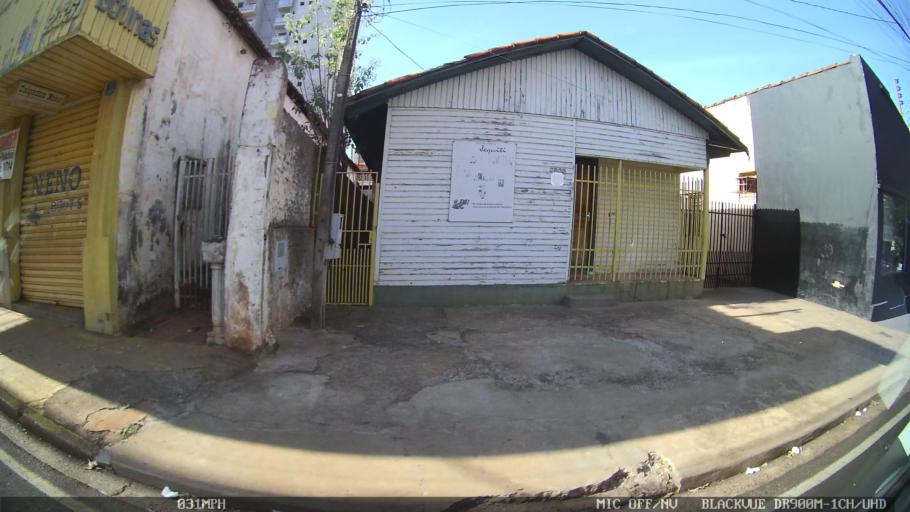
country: BR
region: Sao Paulo
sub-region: Sao Jose Do Rio Preto
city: Sao Jose do Rio Preto
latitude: -20.8056
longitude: -49.3827
